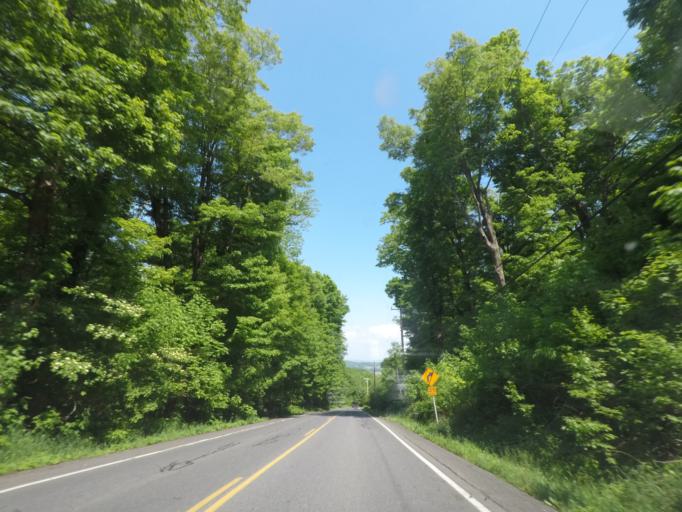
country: US
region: New York
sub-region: Dutchess County
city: Pine Plains
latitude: 41.9681
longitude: -73.5362
